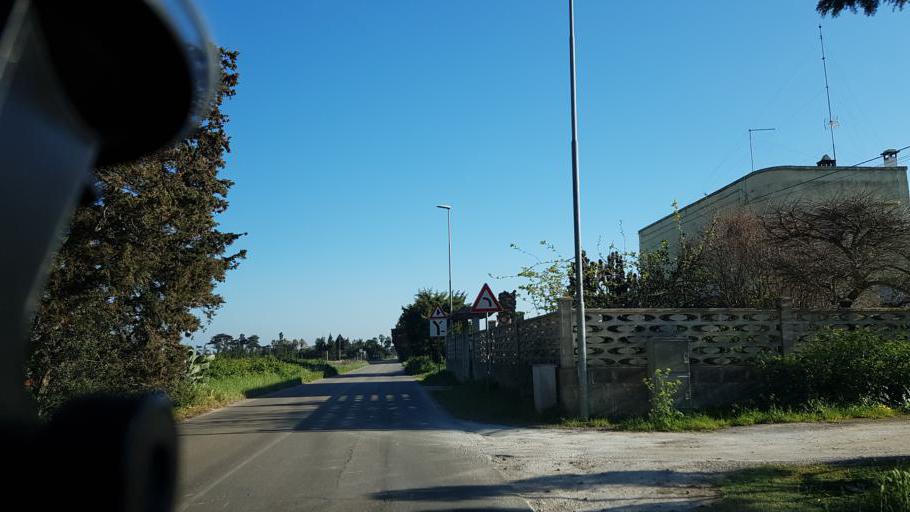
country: IT
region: Apulia
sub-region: Provincia di Lecce
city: Giorgilorio
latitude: 40.4451
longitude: 18.2308
